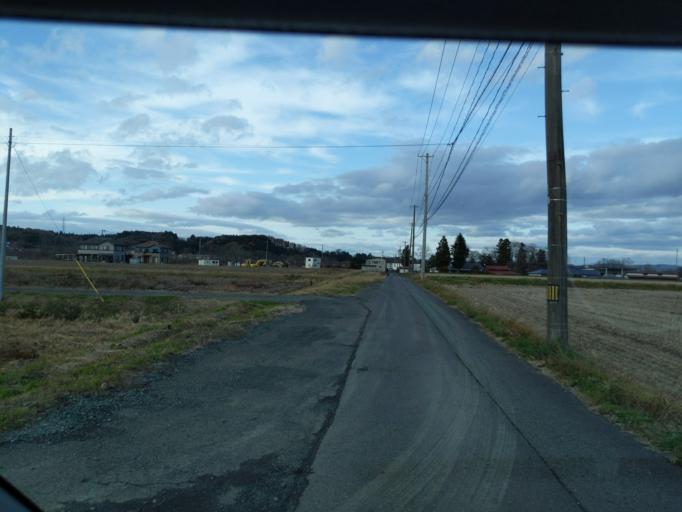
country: JP
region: Iwate
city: Mizusawa
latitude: 39.1604
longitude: 141.0892
